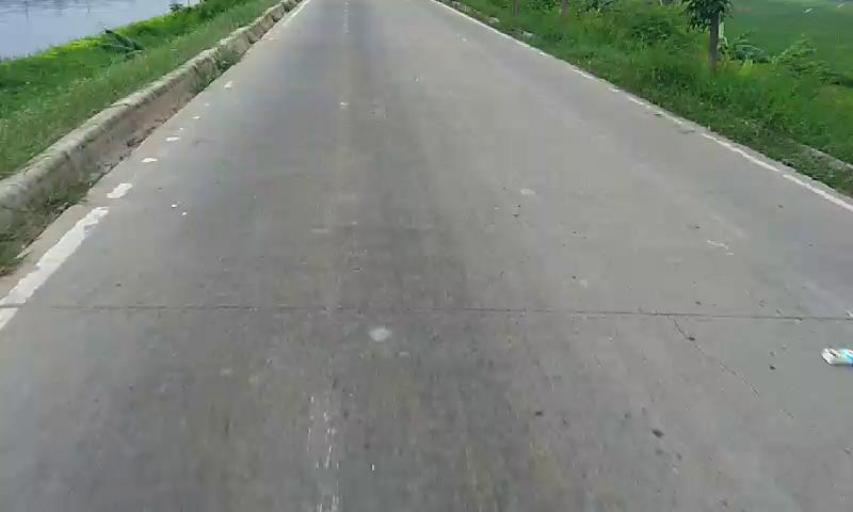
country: ID
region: West Java
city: Bekasi
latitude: -6.1421
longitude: 106.9699
